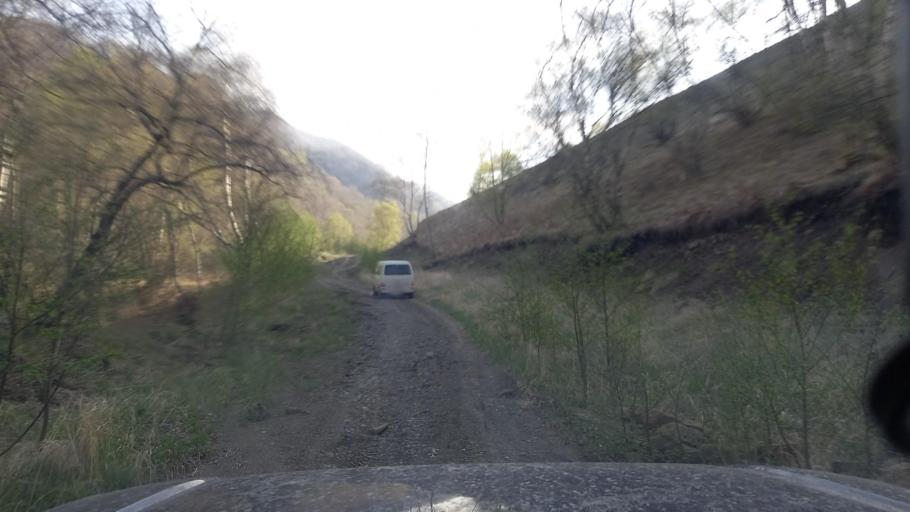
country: RU
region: Kabardino-Balkariya
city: Kamennomostskoye
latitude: 43.6994
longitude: 42.8424
